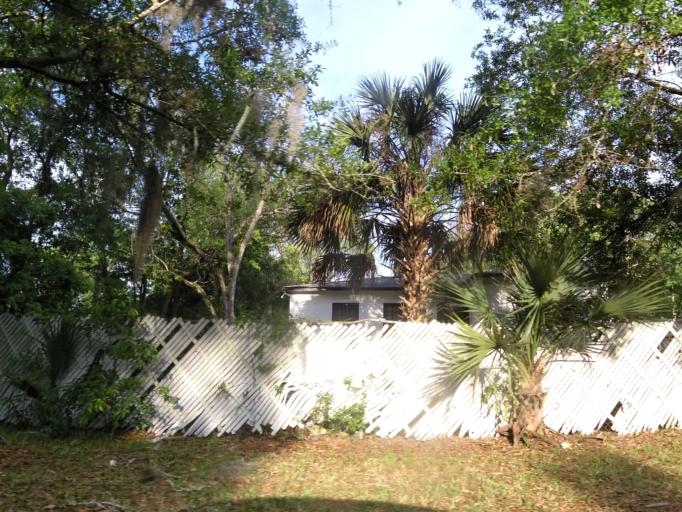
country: US
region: Florida
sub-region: Duval County
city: Jacksonville
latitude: 30.3582
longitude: -81.6776
